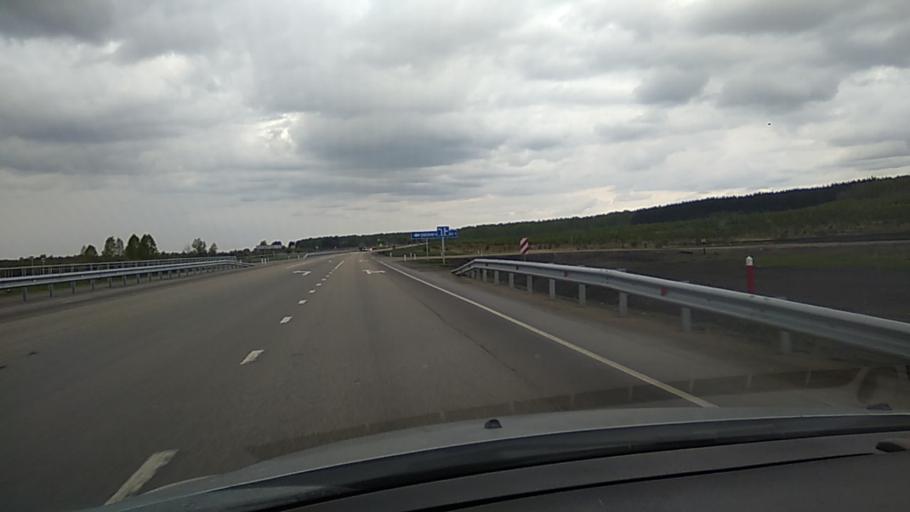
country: RU
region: Kurgan
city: Kataysk
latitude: 56.2969
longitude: 62.4117
